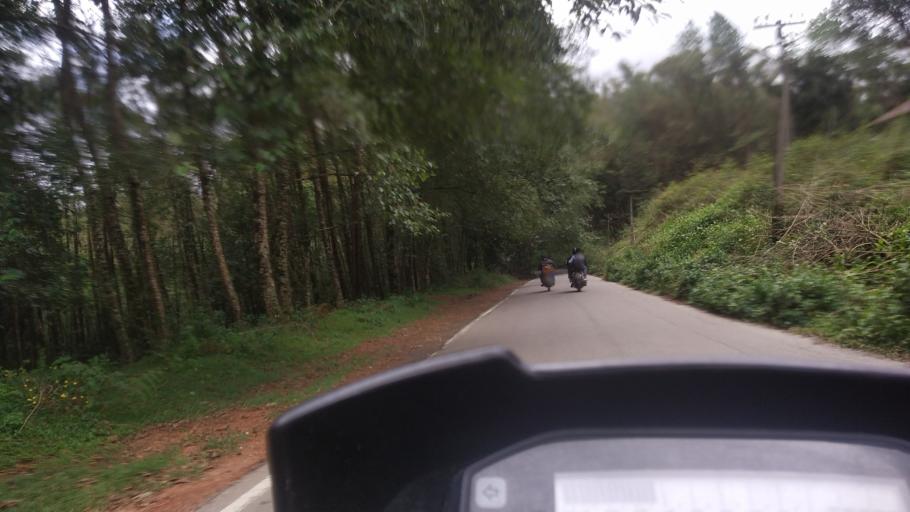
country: IN
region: Kerala
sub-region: Idukki
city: Munnar
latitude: 10.0680
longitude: 77.0984
